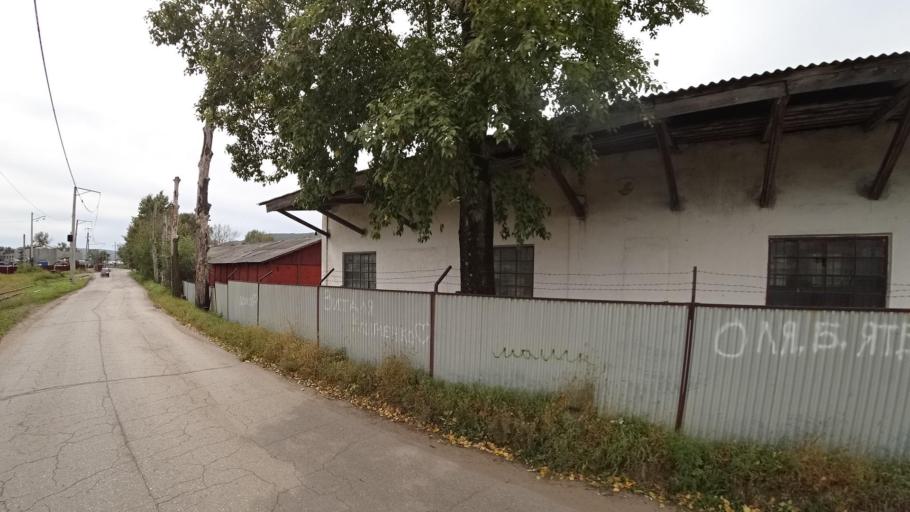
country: RU
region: Jewish Autonomous Oblast
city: Khingansk
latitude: 49.0199
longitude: 131.0548
